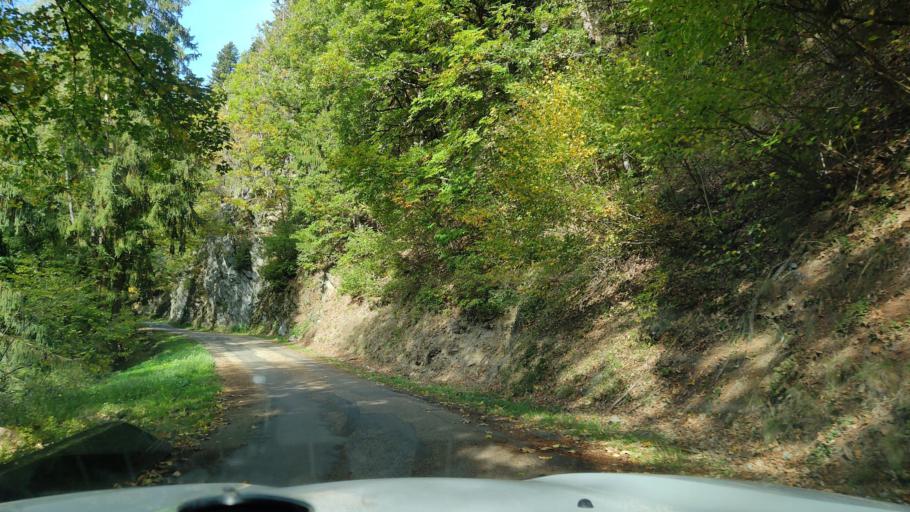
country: FR
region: Rhone-Alpes
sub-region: Departement de la Savoie
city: Beaufort
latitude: 45.7258
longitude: 6.5057
